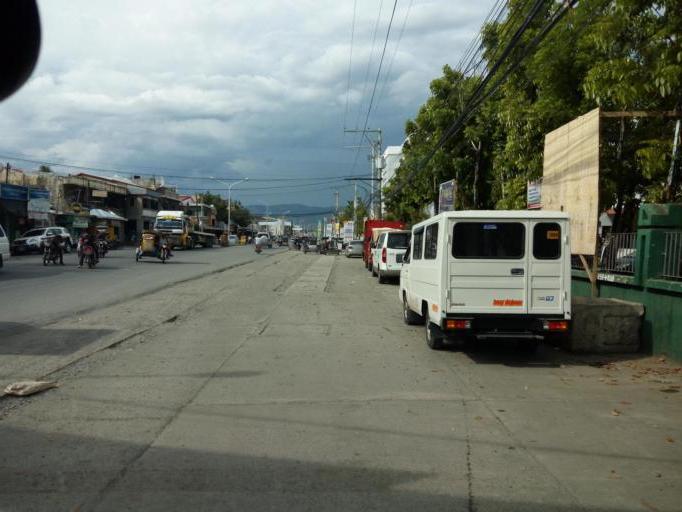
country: PH
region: Central Luzon
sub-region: Province of Nueva Ecija
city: Sibul
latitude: 15.7952
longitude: 120.9927
